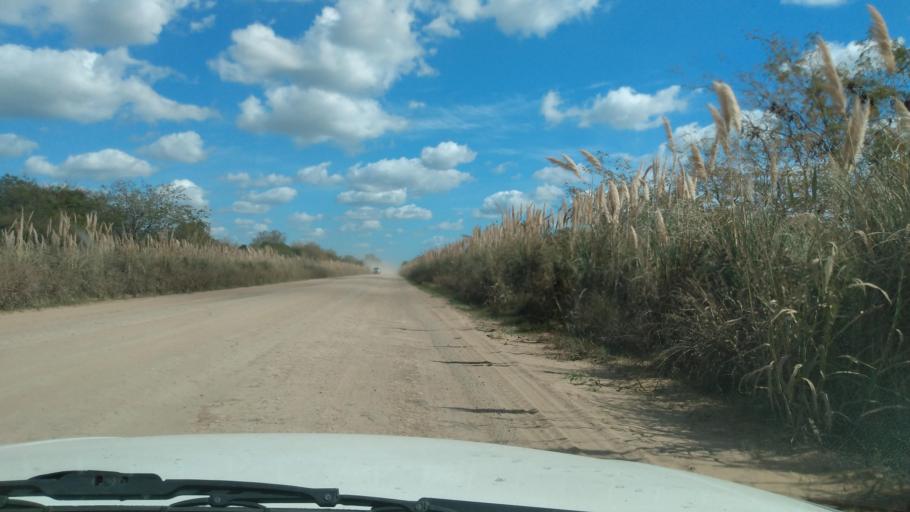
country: AR
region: Buenos Aires
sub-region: Partido de Navarro
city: Navarro
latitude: -34.9987
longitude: -59.3276
